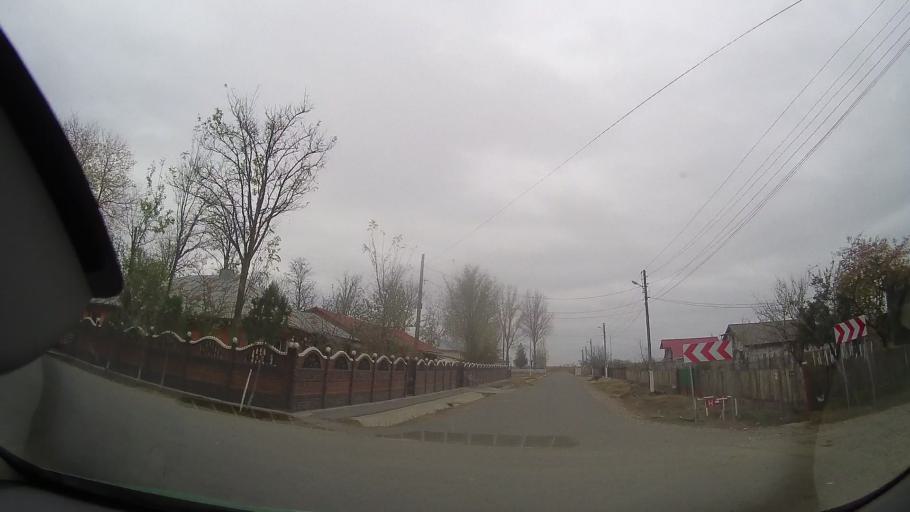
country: RO
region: Braila
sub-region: Comuna Rosiori
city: Rosiori
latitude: 44.8308
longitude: 27.3363
